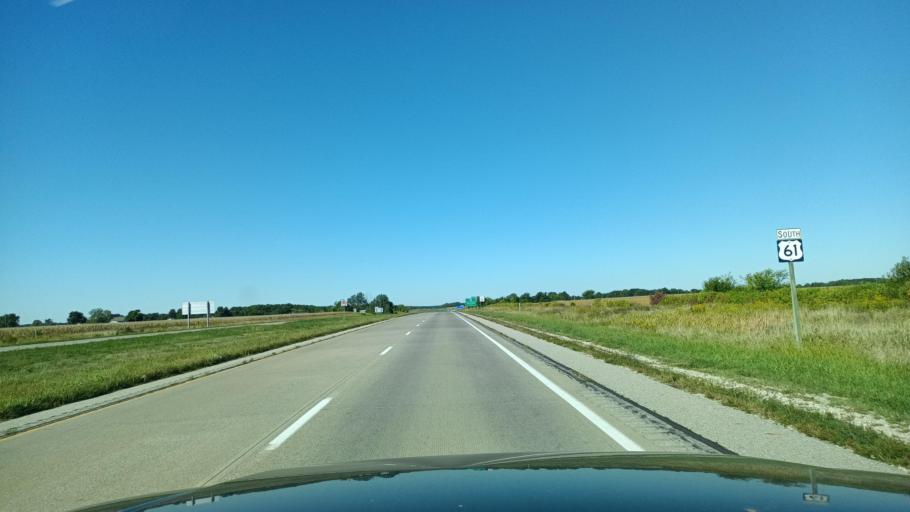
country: US
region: Iowa
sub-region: Lee County
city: Fort Madison
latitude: 40.6706
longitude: -91.3369
